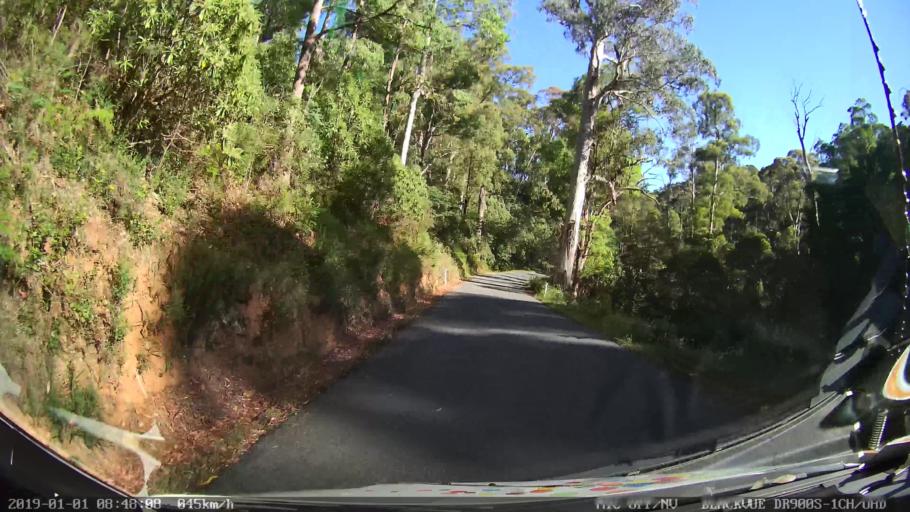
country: AU
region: New South Wales
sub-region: Snowy River
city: Jindabyne
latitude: -36.2906
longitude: 148.1992
